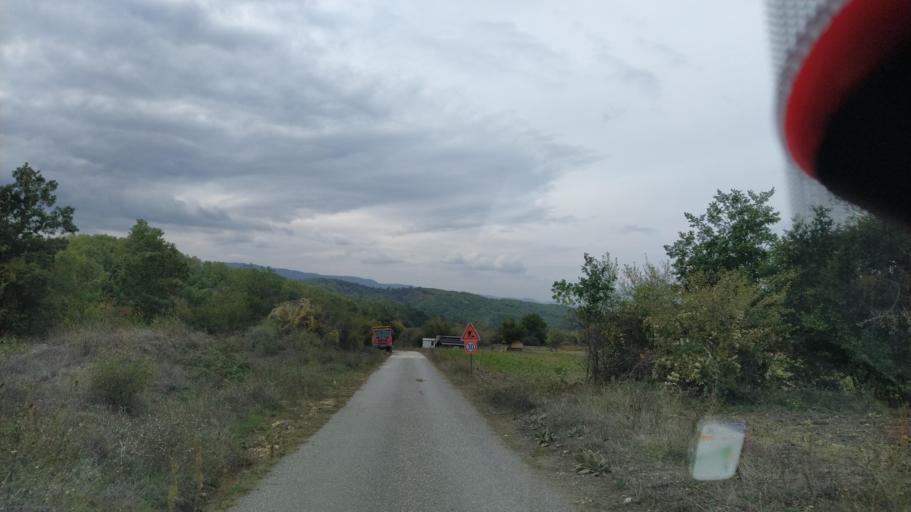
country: MK
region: Konce
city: Konce
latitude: 41.5073
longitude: 22.4656
